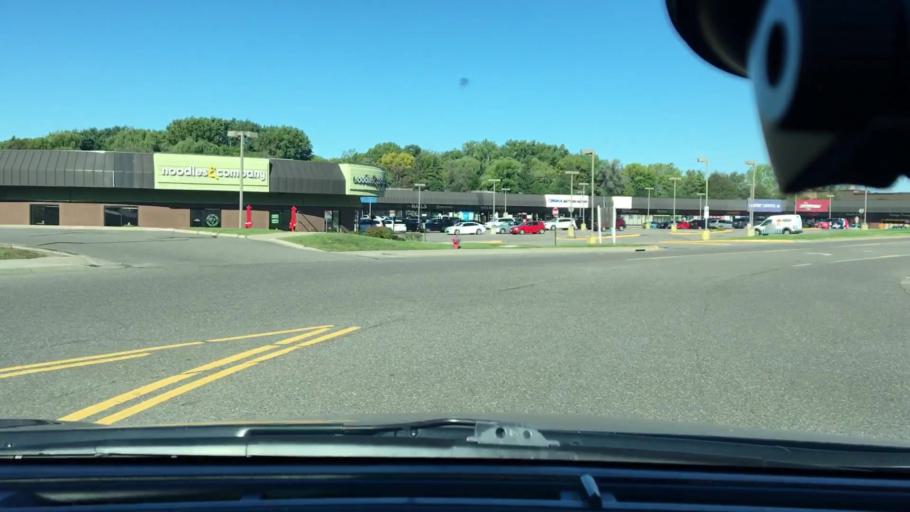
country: US
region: Minnesota
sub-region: Hennepin County
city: Minnetonka Mills
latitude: 44.9659
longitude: -93.4435
